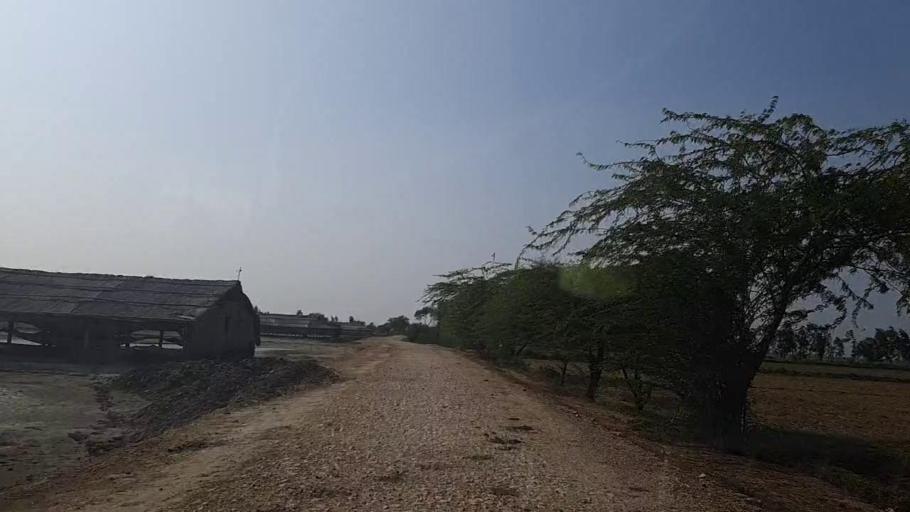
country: PK
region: Sindh
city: Mirpur Sakro
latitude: 24.5675
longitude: 67.8234
